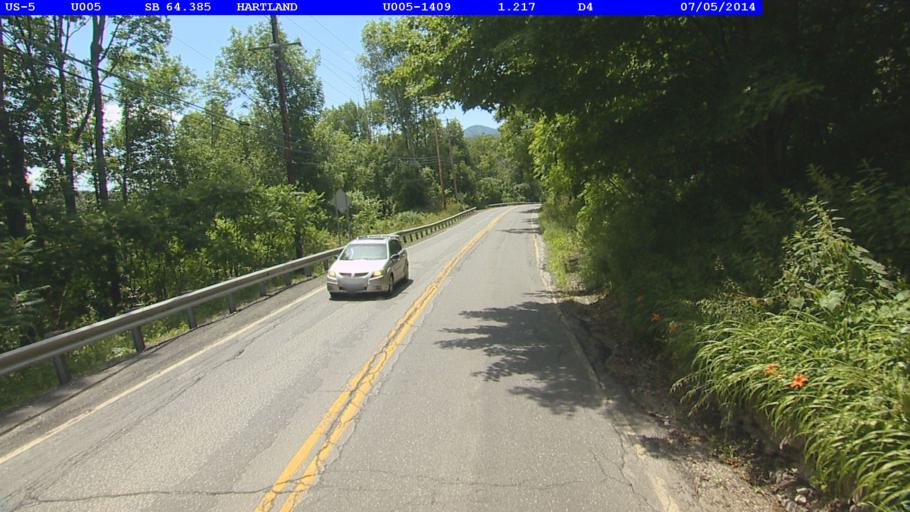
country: US
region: Vermont
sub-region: Windsor County
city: Windsor
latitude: 43.5360
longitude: -72.4022
